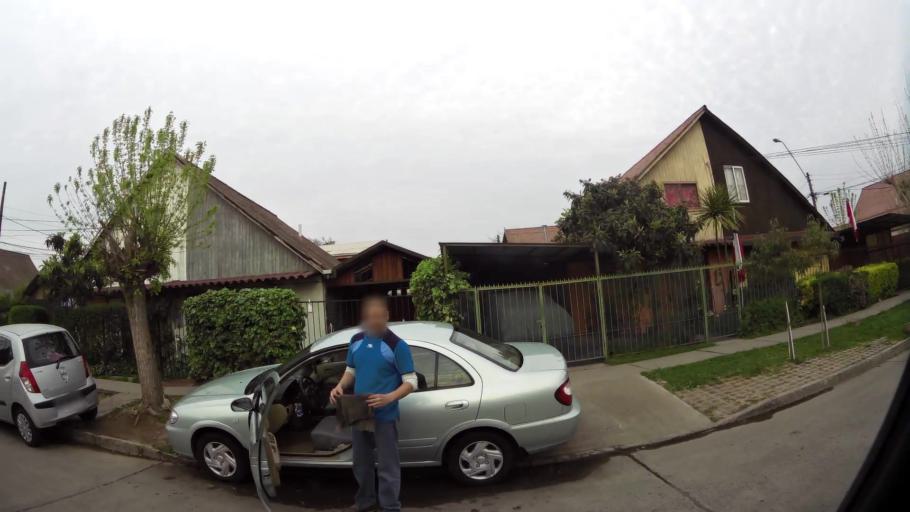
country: CL
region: Santiago Metropolitan
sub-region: Provincia de Santiago
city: Lo Prado
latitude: -33.5259
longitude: -70.7704
